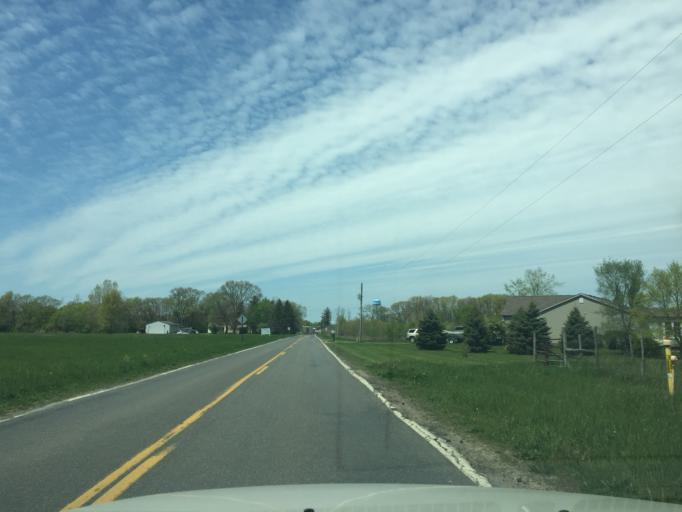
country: US
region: Michigan
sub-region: Berrien County
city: Stevensville
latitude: 41.9513
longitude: -86.4809
